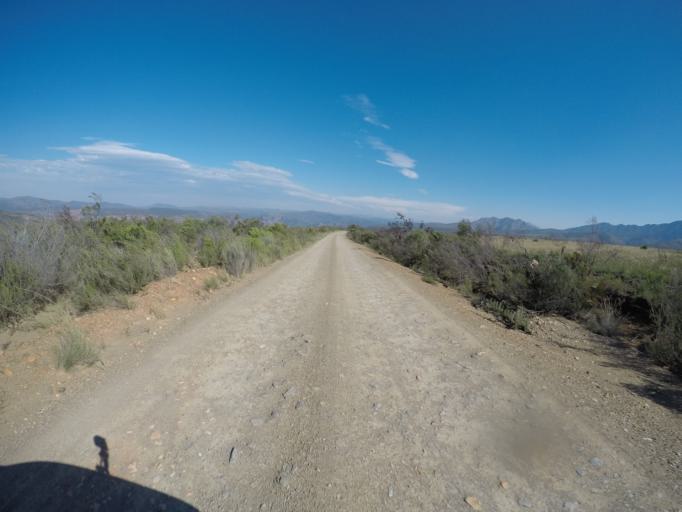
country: ZA
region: Eastern Cape
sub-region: Cacadu District Municipality
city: Kareedouw
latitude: -33.6345
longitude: 24.4748
